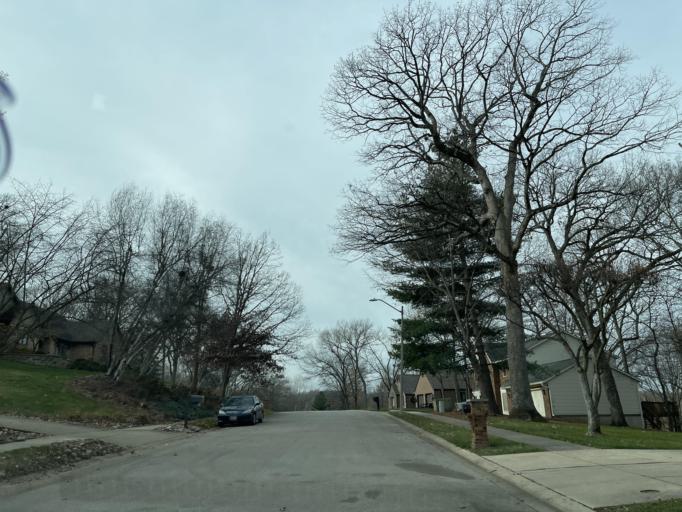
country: US
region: Illinois
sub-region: Sangamon County
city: Leland Grove
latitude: 39.8091
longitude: -89.7272
